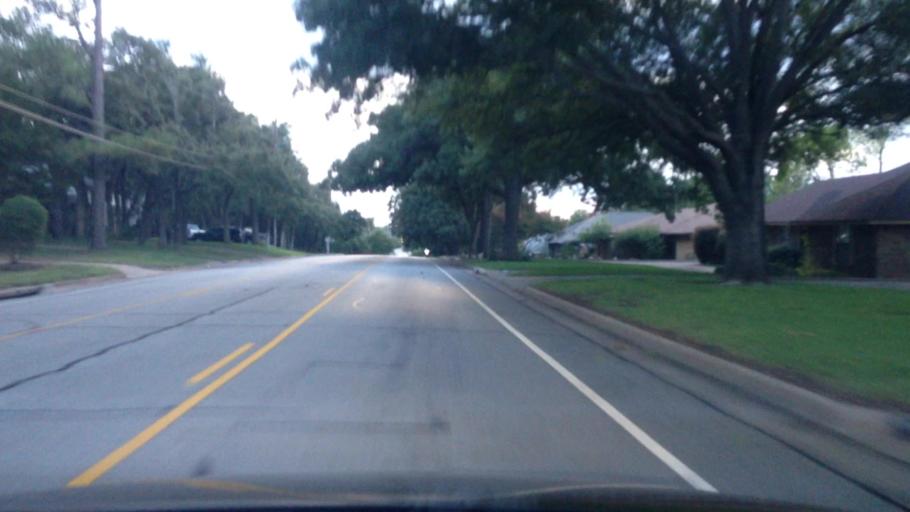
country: US
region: Texas
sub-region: Tarrant County
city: Arlington
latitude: 32.7318
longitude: -97.1340
